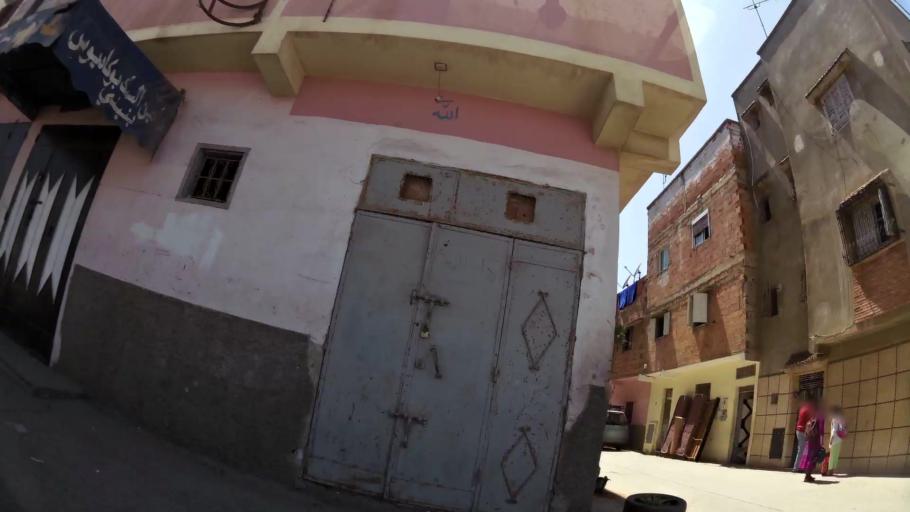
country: MA
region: Rabat-Sale-Zemmour-Zaer
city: Sale
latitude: 34.0615
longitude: -6.7783
